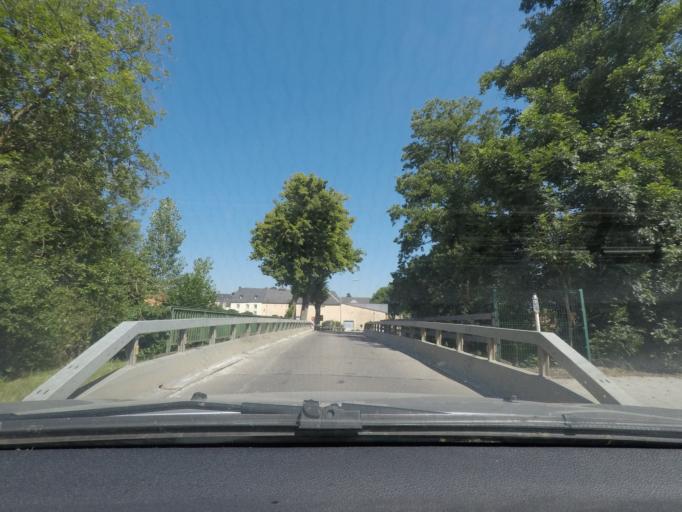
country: LU
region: Diekirch
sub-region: Canton de Redange
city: Ell
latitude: 49.7623
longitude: 5.8588
